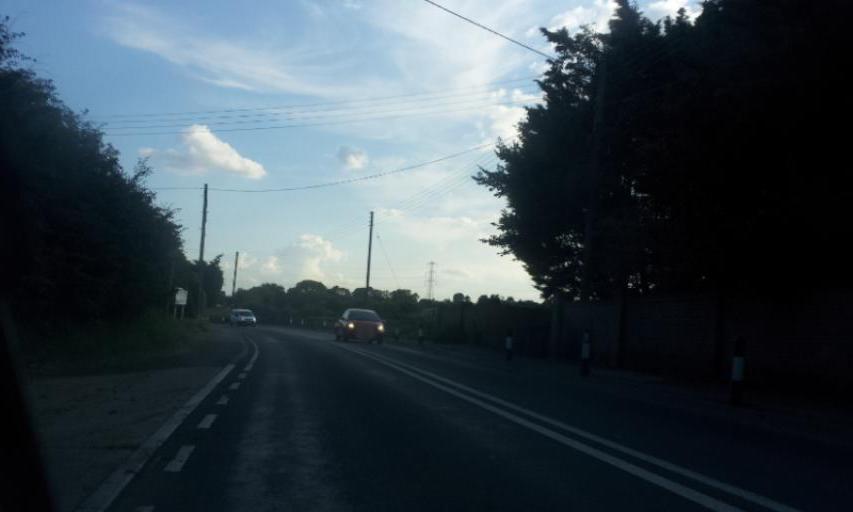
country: GB
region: England
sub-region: Kent
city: Longfield
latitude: 51.4070
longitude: 0.2821
